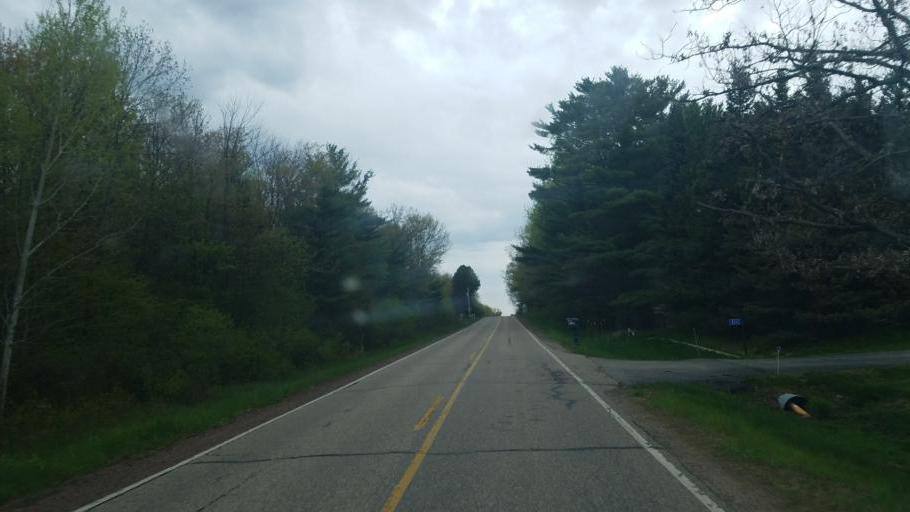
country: US
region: Wisconsin
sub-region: Wood County
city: Marshfield
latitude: 44.5463
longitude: -90.2999
